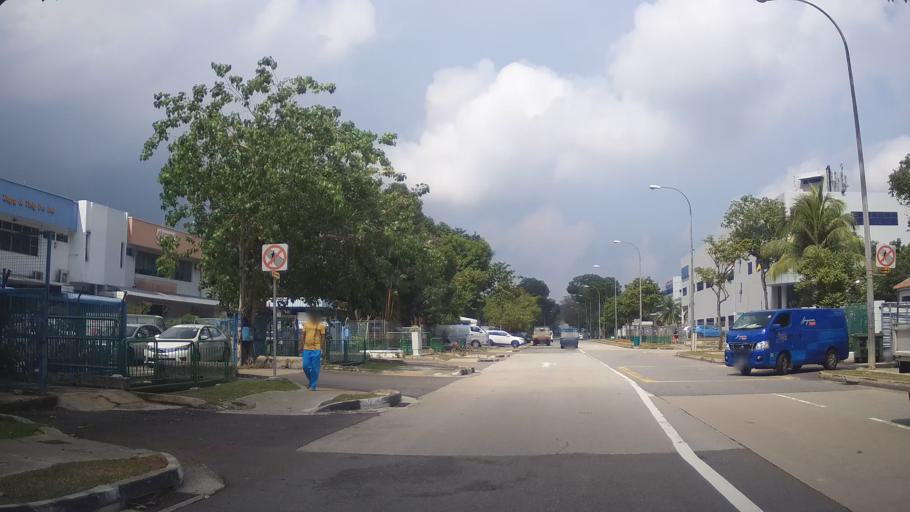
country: MY
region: Johor
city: Johor Bahru
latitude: 1.3318
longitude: 103.6959
